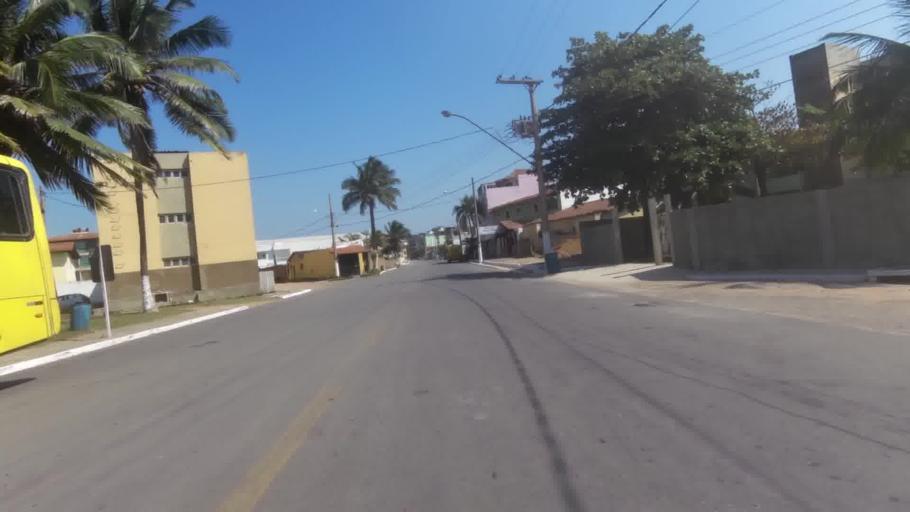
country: BR
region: Espirito Santo
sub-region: Marataizes
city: Marataizes
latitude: -21.0497
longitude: -40.8312
